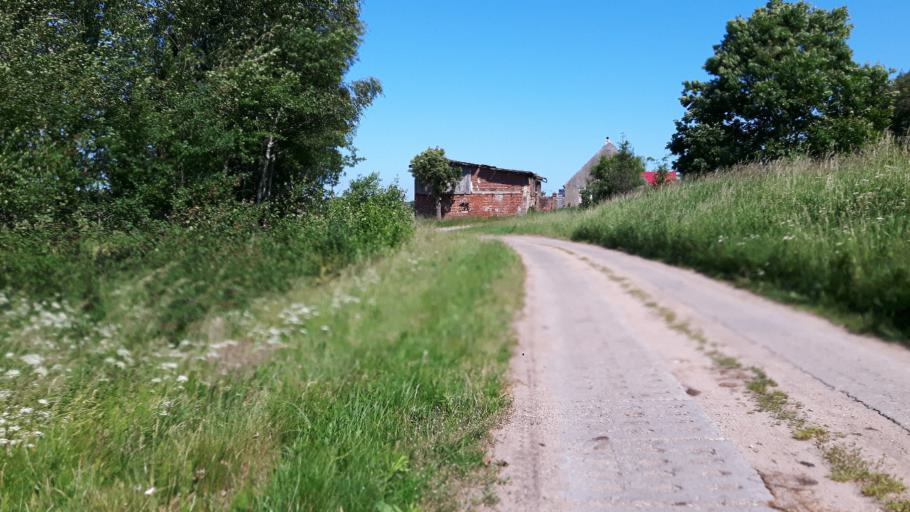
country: PL
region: Pomeranian Voivodeship
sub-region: Powiat slupski
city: Glowczyce
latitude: 54.6419
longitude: 17.3656
